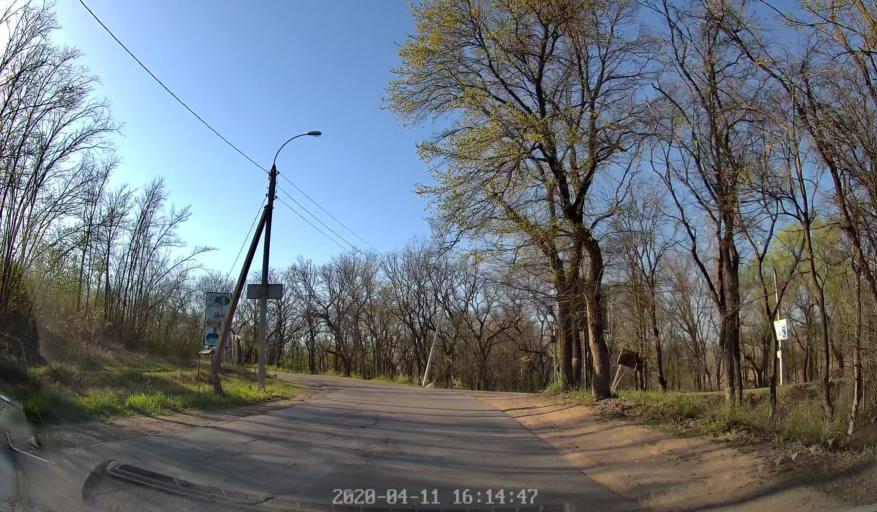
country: MD
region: Chisinau
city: Vadul lui Voda
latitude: 47.0774
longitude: 29.0989
